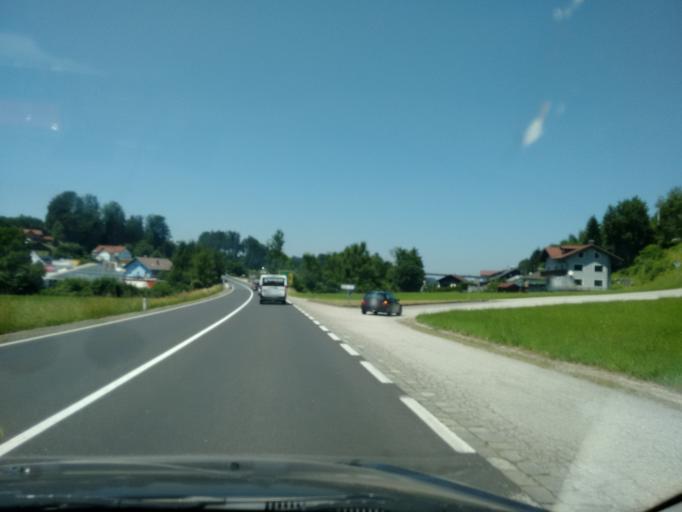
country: AT
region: Upper Austria
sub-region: Politischer Bezirk Gmunden
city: Altmunster
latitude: 47.9490
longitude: 13.7521
